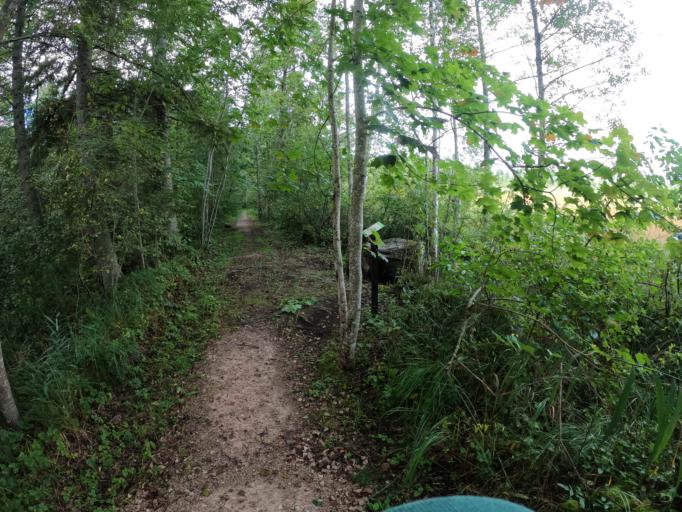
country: LV
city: Tireli
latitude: 56.9603
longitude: 23.5435
